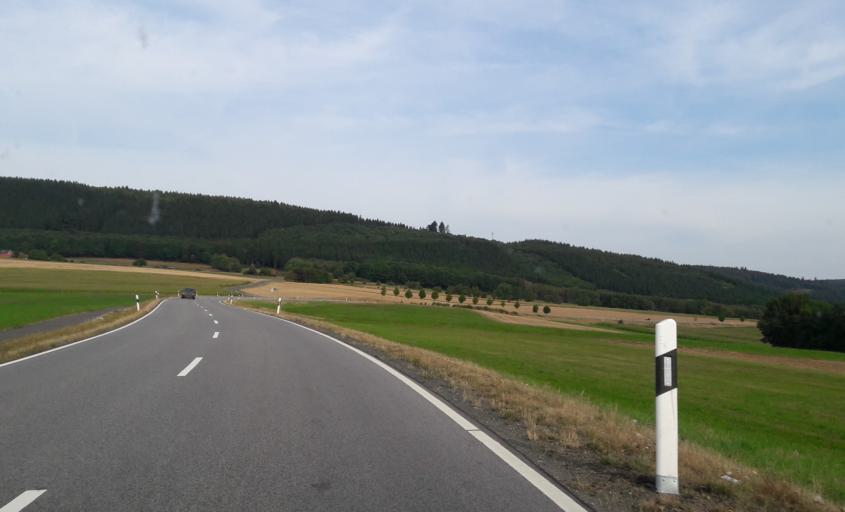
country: DE
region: Rheinland-Pfalz
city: Rinzenberg
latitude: 49.6746
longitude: 7.1460
